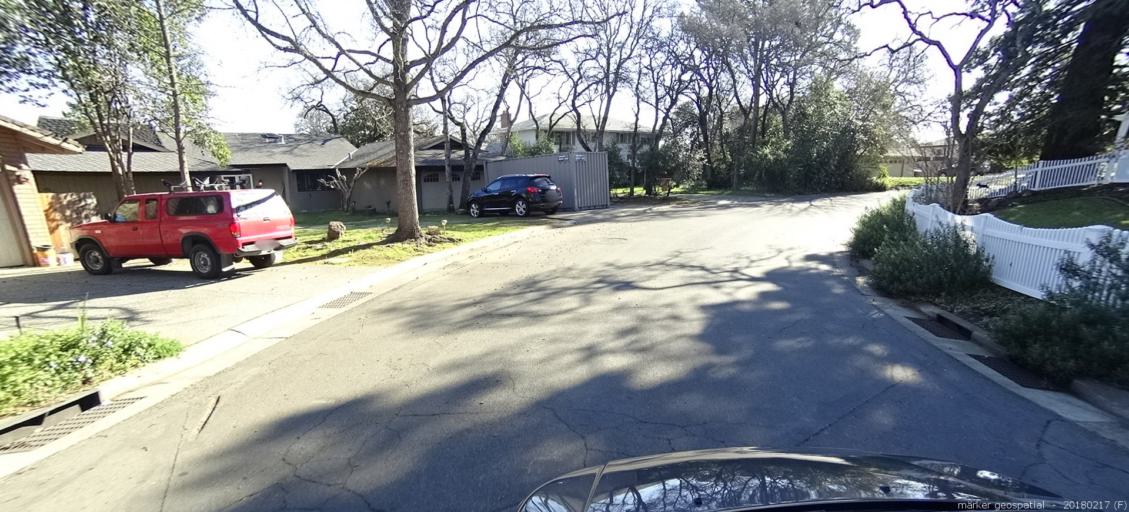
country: US
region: California
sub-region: Sacramento County
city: Folsom
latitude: 38.6648
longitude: -121.1949
